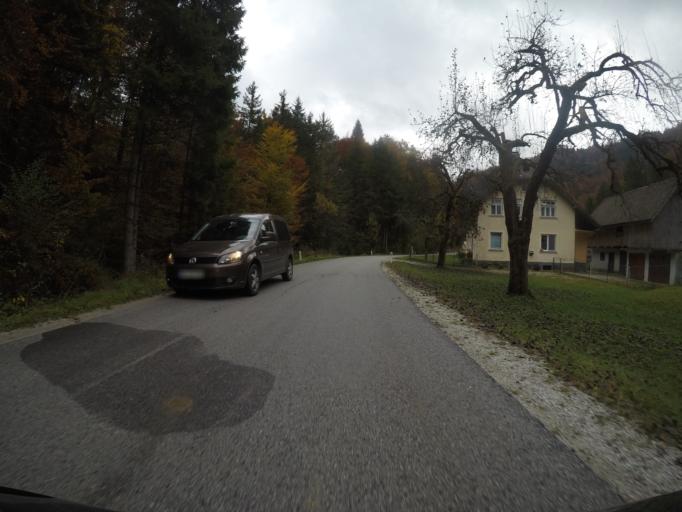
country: SI
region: Gorje
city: Zgornje Gorje
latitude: 46.3865
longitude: 14.0298
